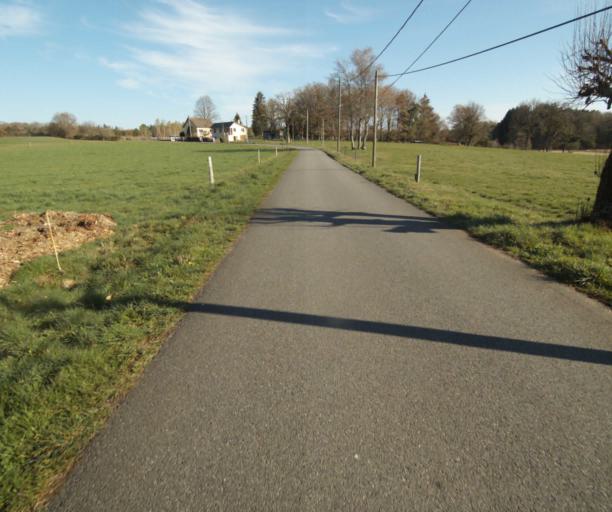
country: FR
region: Limousin
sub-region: Departement de la Correze
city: Correze
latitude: 45.3191
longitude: 1.8884
